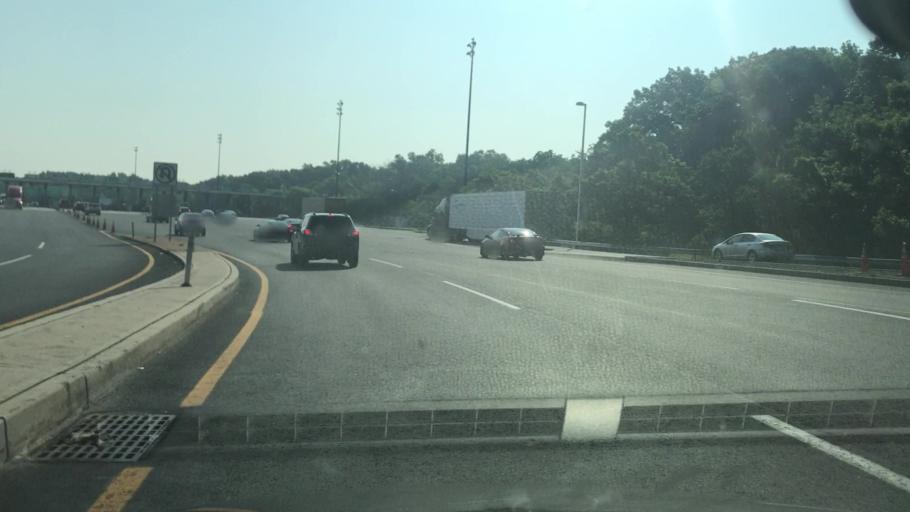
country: US
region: New Jersey
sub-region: Middlesex County
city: Fords
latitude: 40.5240
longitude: -74.3406
